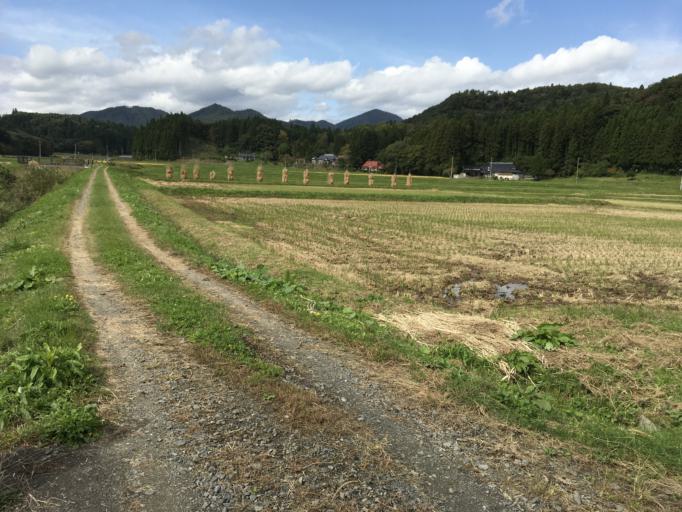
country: JP
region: Iwate
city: Ichinoseki
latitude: 38.9763
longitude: 140.9558
